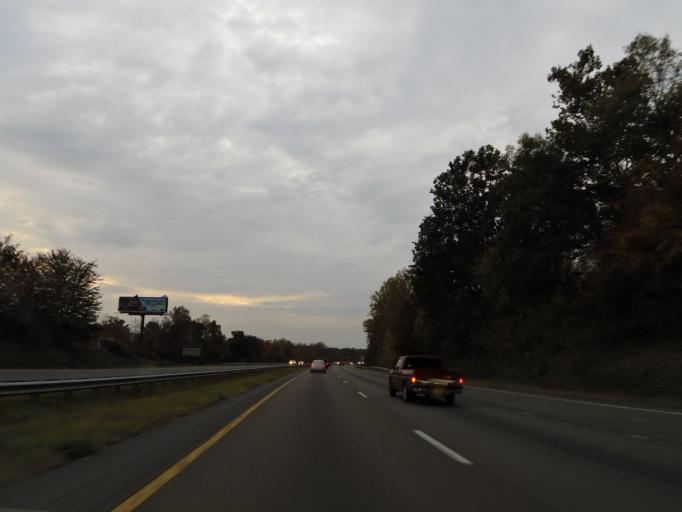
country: US
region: North Carolina
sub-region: Burke County
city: Hildebran
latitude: 35.7059
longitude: -81.4277
